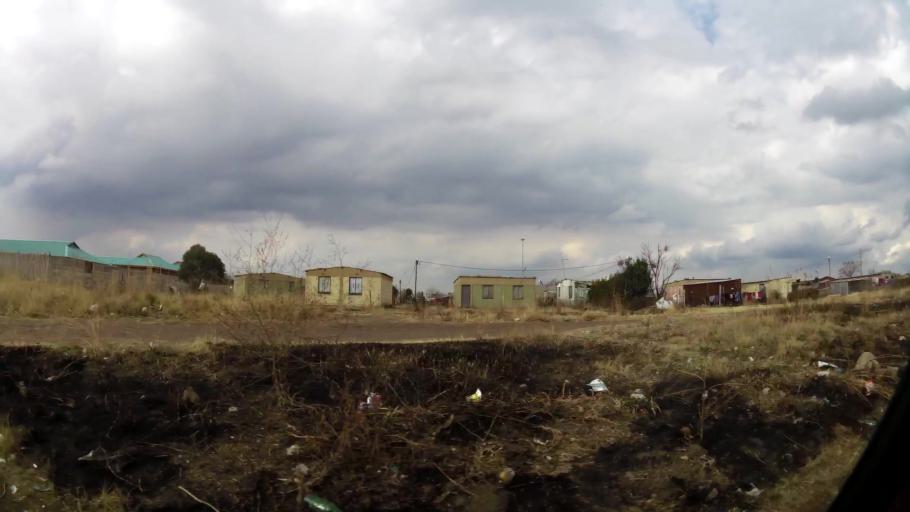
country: ZA
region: Gauteng
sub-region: Sedibeng District Municipality
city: Vanderbijlpark
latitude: -26.6922
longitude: 27.7841
